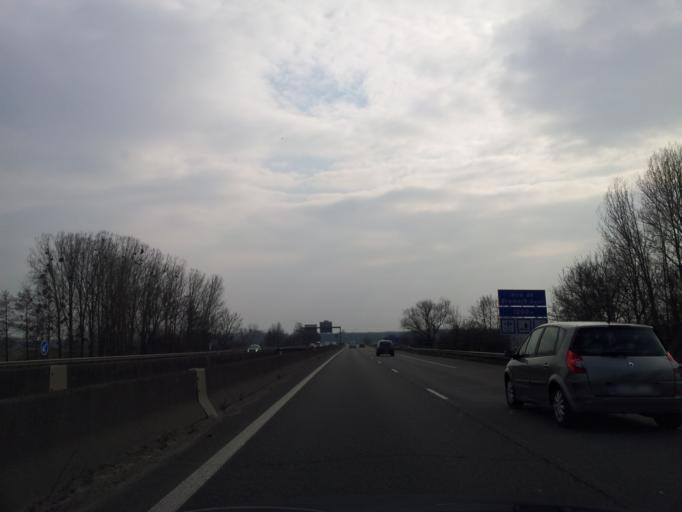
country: FR
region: Alsace
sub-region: Departement du Bas-Rhin
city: Brumath
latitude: 48.7376
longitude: 7.6883
